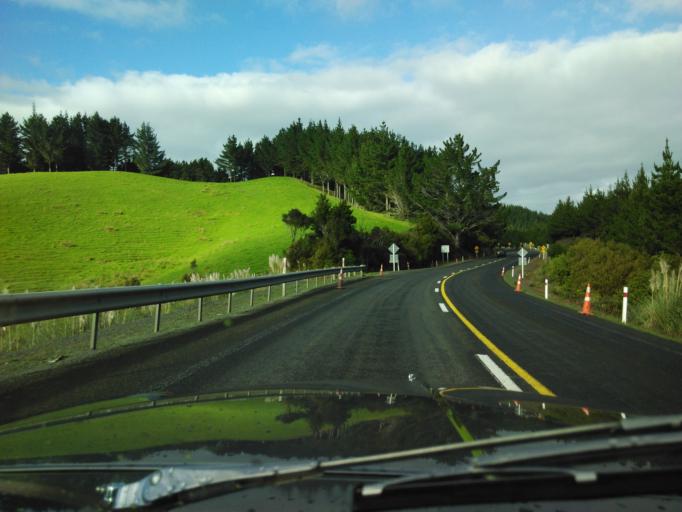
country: NZ
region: Auckland
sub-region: Auckland
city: Wellsford
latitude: -36.2245
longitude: 174.4894
